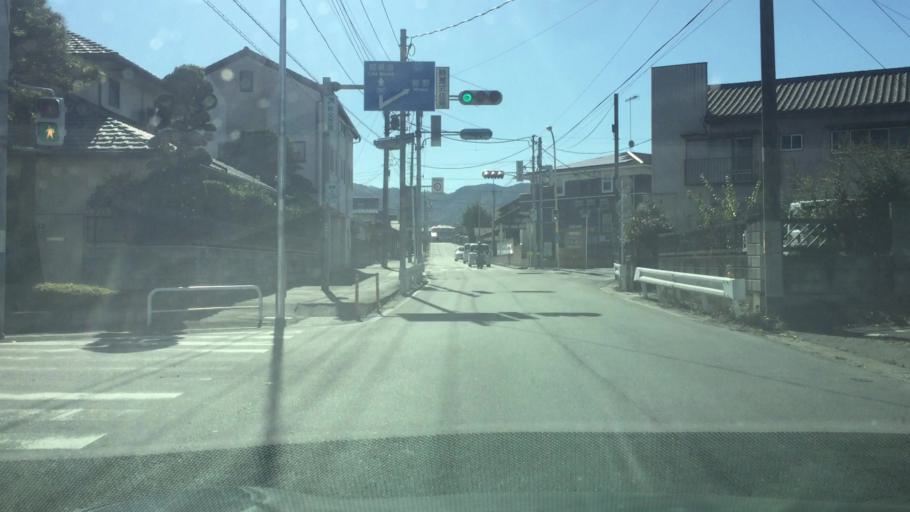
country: JP
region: Saitama
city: Kodamacho-kodamaminami
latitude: 36.1868
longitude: 139.1291
